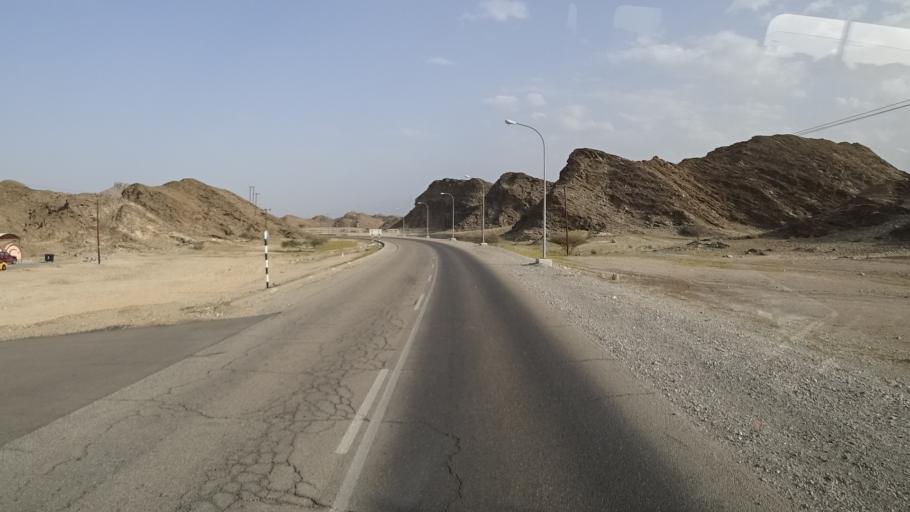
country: OM
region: Muhafazat Masqat
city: Bawshar
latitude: 23.3728
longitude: 58.5175
